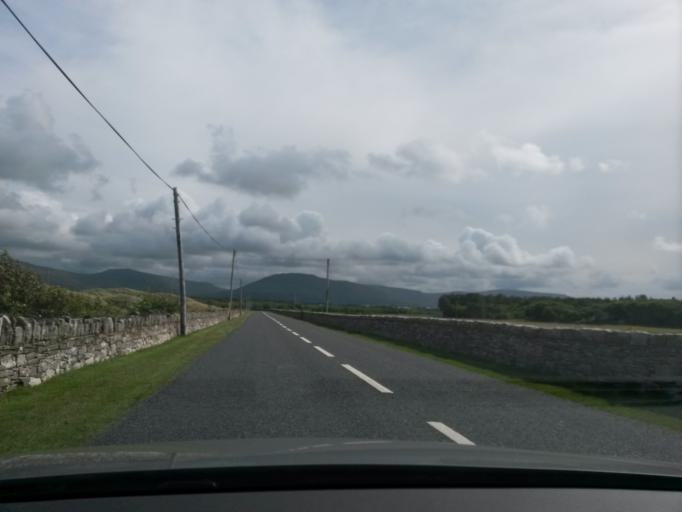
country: IE
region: Connaught
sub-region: County Leitrim
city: Kinlough
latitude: 54.4548
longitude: -8.4547
